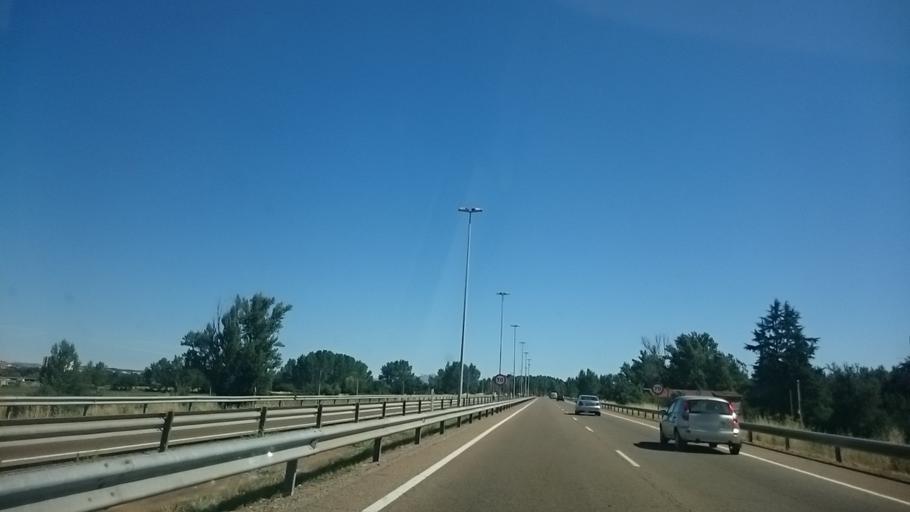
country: ES
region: Castille and Leon
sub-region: Provincia de Leon
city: Leon
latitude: 42.5928
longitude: -5.5528
